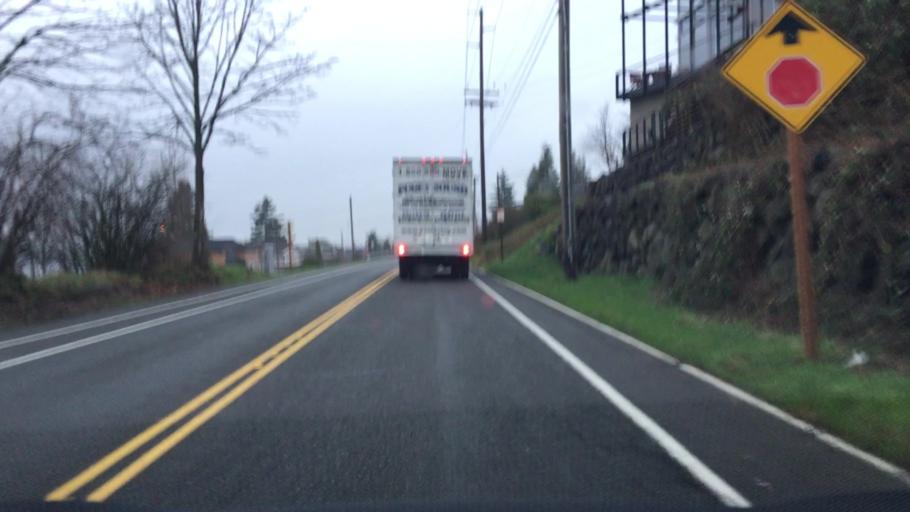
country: US
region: Washington
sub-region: King County
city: Renton
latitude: 47.5224
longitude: -122.2076
